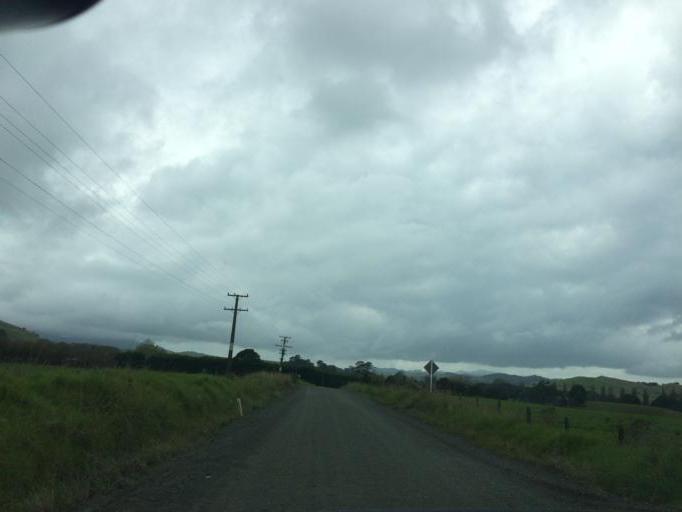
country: NZ
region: Northland
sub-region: Kaipara District
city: Dargaville
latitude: -35.8308
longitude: 173.8413
